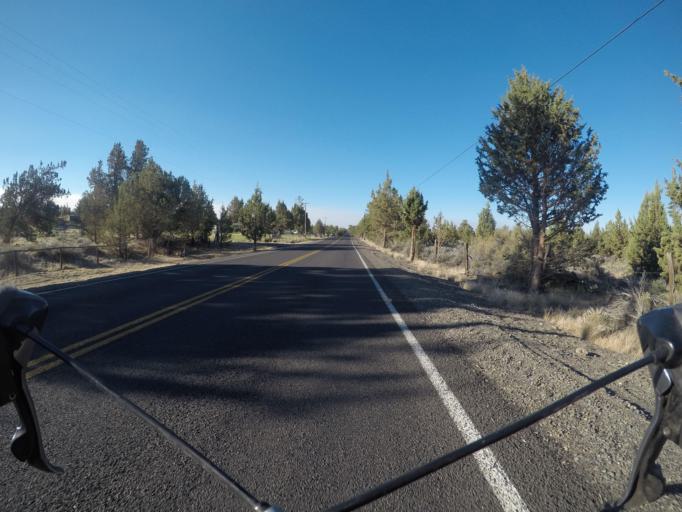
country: US
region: Oregon
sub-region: Deschutes County
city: Redmond
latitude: 44.2533
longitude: -121.2396
